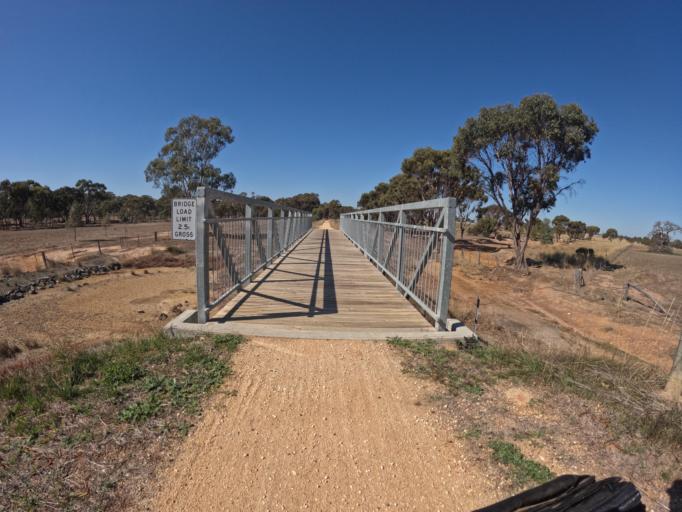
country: AU
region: Victoria
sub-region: Greater Bendigo
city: Kennington
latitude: -36.8297
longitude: 144.5898
